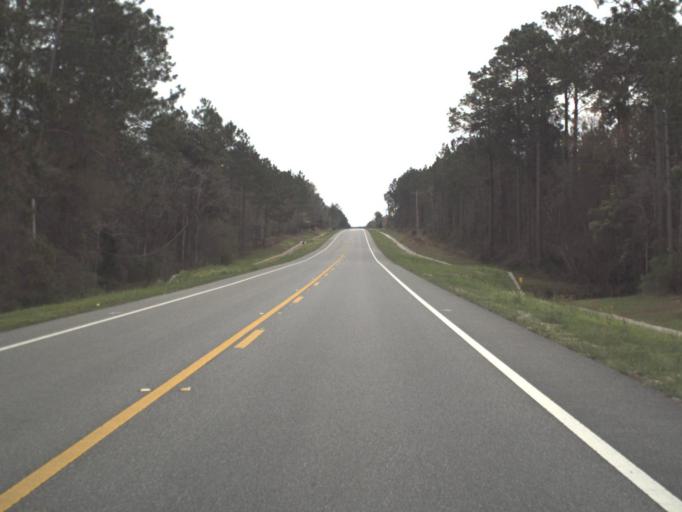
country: US
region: Florida
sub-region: Gulf County
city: Wewahitchka
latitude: 30.2498
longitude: -85.2285
